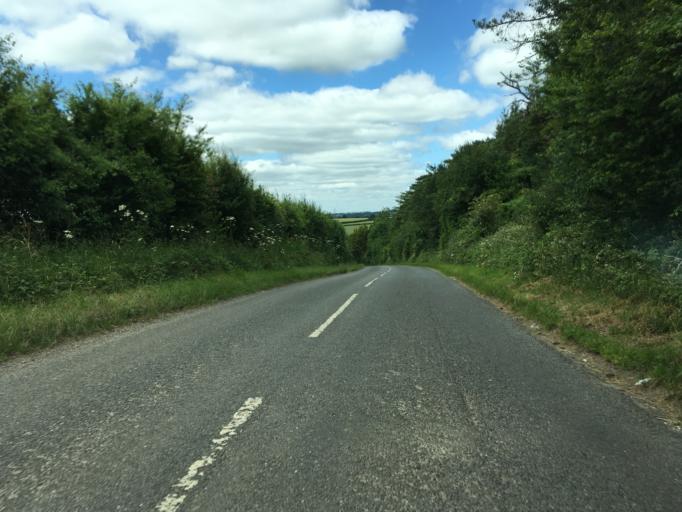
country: GB
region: England
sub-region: Hampshire
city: Overton
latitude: 51.2435
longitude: -1.3562
